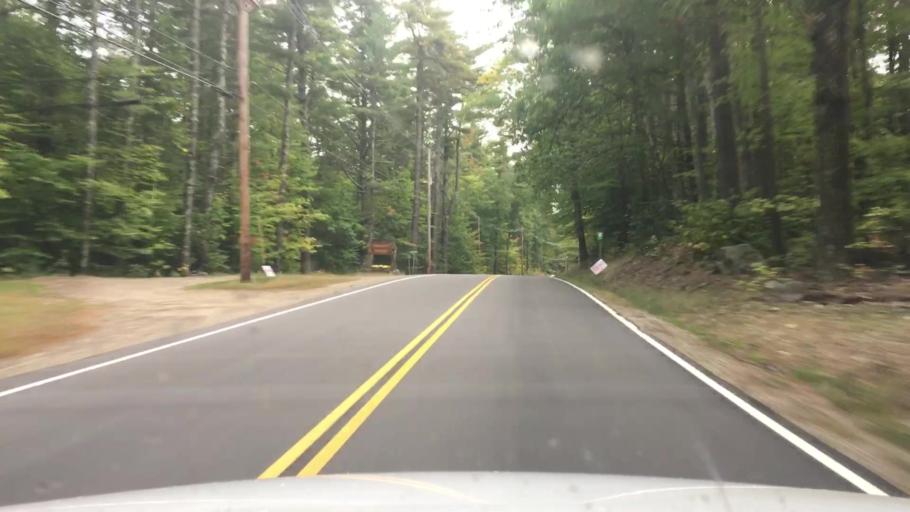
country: US
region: New Hampshire
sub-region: Belknap County
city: Gilford
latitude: 43.5457
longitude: -71.3041
